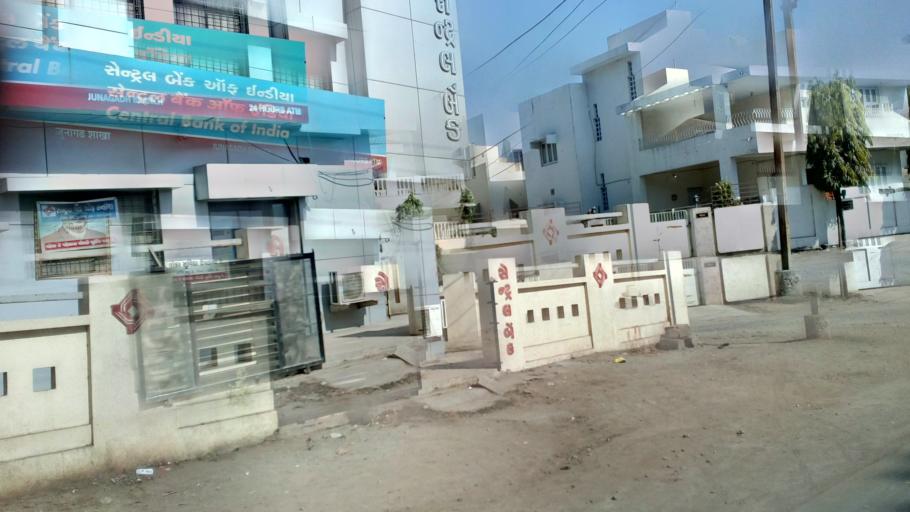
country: IN
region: Punjab
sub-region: Ludhiana
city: Ludhiana
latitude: 30.9374
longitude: 75.8374
